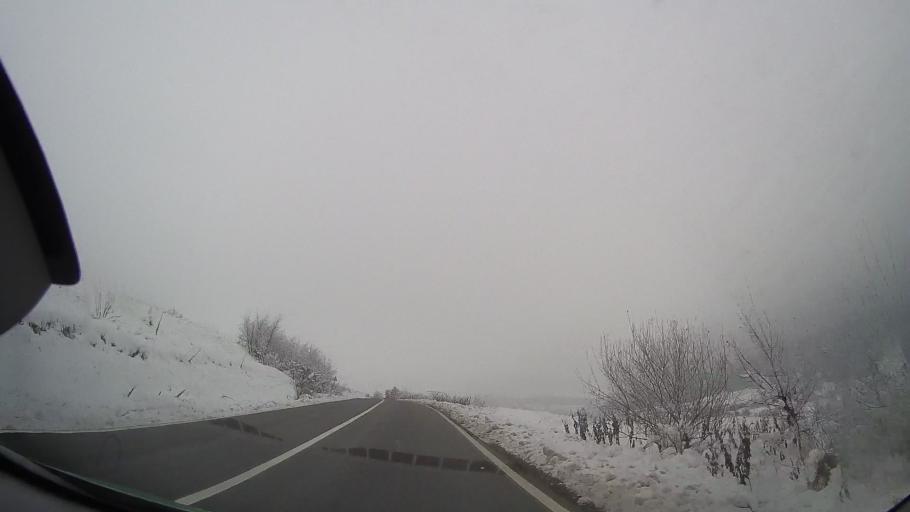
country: RO
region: Neamt
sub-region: Comuna Poenari
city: Poienari
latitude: 46.8730
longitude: 27.1396
